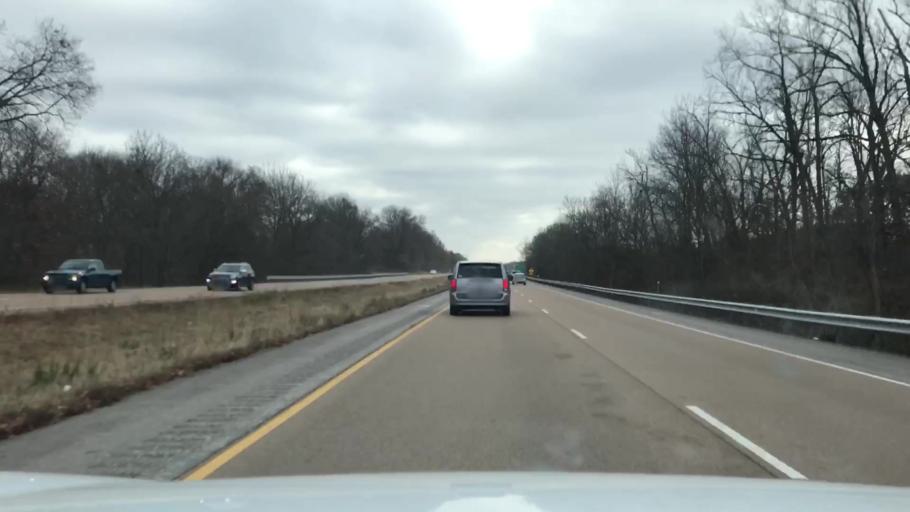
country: US
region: Illinois
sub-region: Saint Clair County
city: Belleville
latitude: 38.5113
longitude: -90.0150
